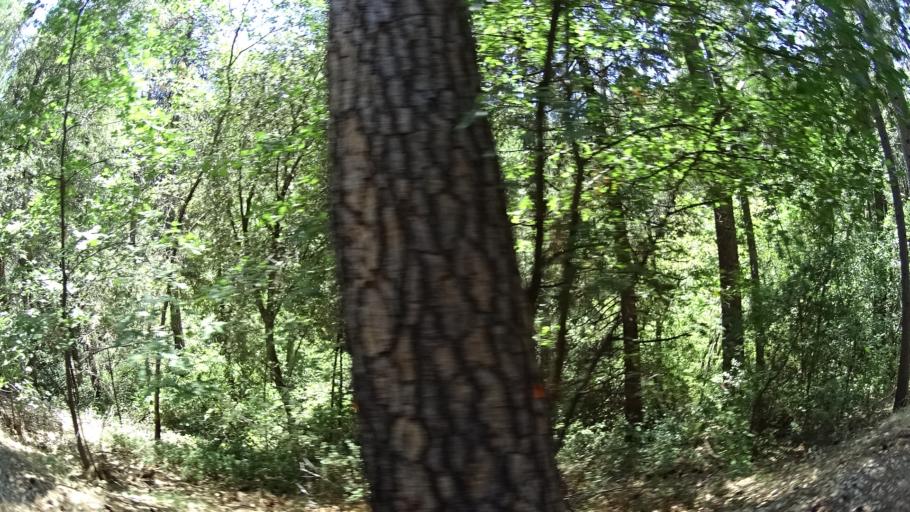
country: US
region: California
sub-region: Calaveras County
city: Forest Meadows
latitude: 38.1498
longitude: -120.4056
